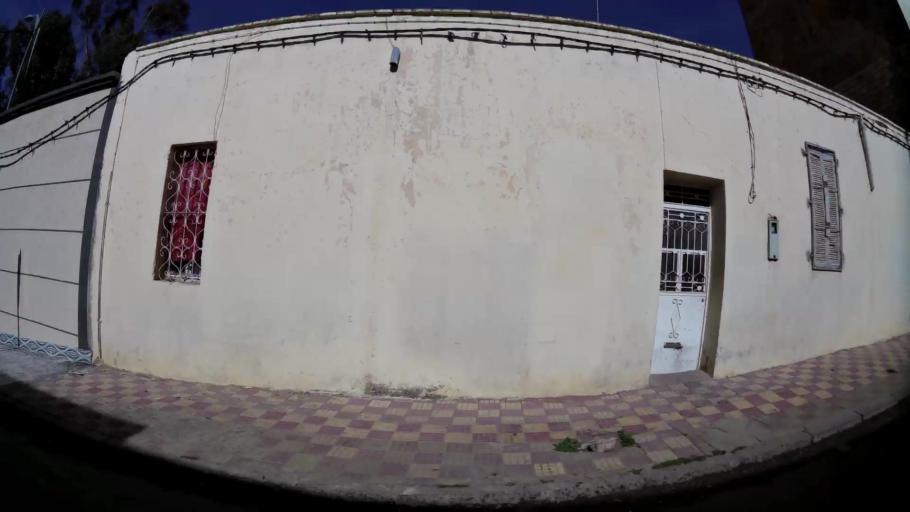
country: MA
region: Oriental
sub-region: Oujda-Angad
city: Oujda
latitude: 34.6724
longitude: -1.9138
